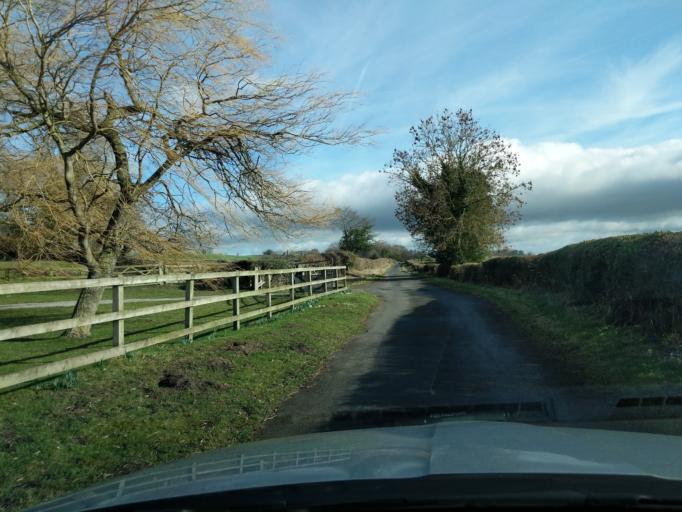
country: GB
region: England
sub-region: North Yorkshire
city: Catterick Garrison
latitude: 54.3348
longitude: -1.7013
